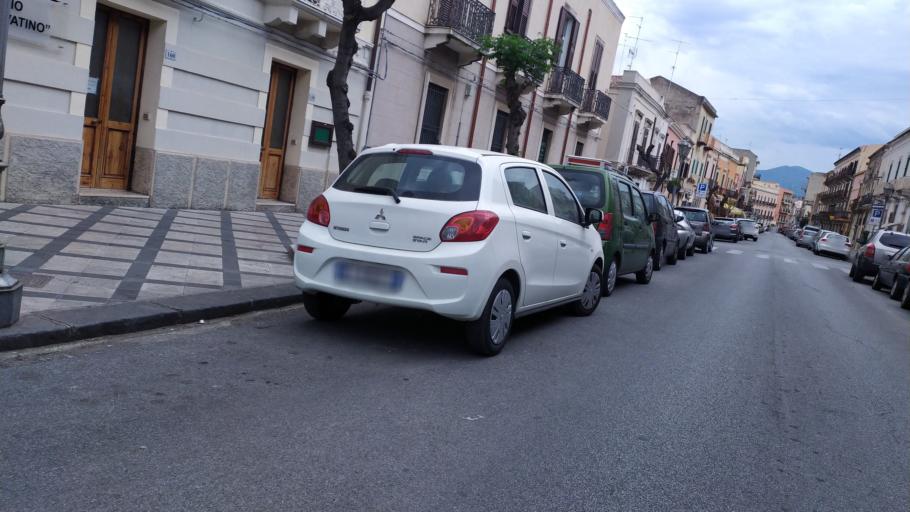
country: IT
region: Sicily
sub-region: Messina
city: Milazzo
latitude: 38.2232
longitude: 15.2407
